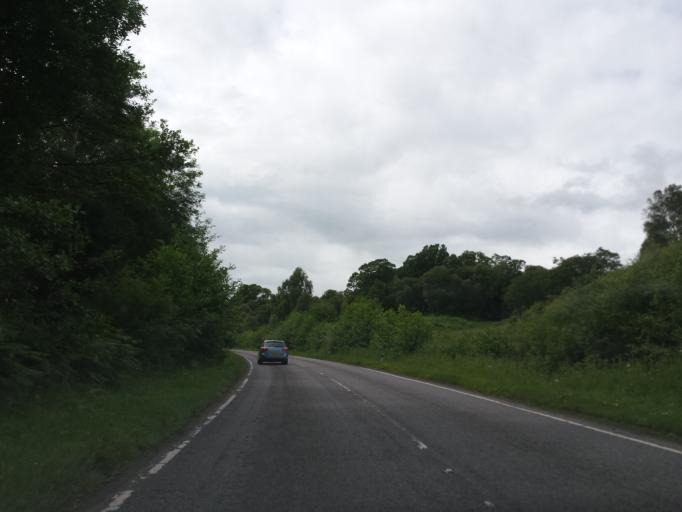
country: GB
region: Scotland
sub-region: Highland
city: Fort William
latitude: 56.8531
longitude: -5.1757
